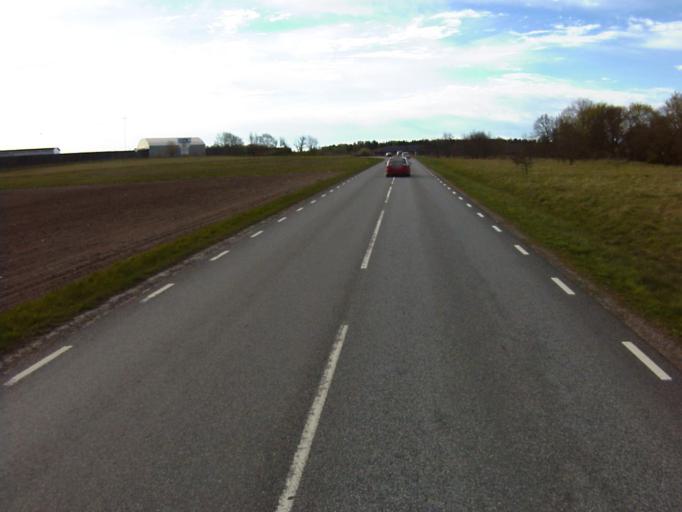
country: SE
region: Skane
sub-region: Kristianstads Kommun
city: Norra Asum
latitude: 55.9957
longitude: 14.1129
